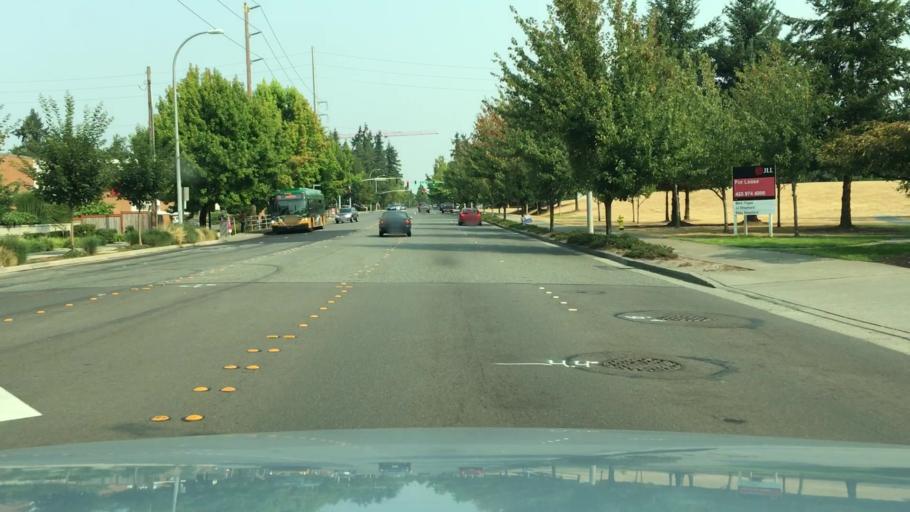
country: US
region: Washington
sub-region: King County
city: Redmond
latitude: 47.6299
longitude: -122.1323
